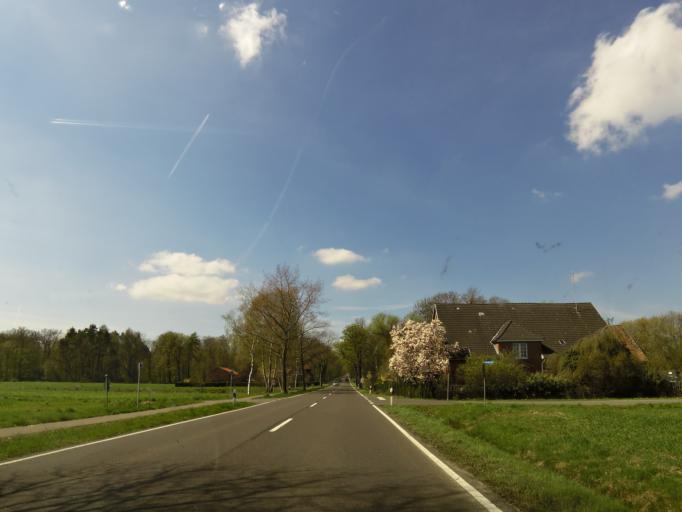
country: DE
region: Lower Saxony
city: Wolpinghausen
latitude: 52.4403
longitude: 9.2446
